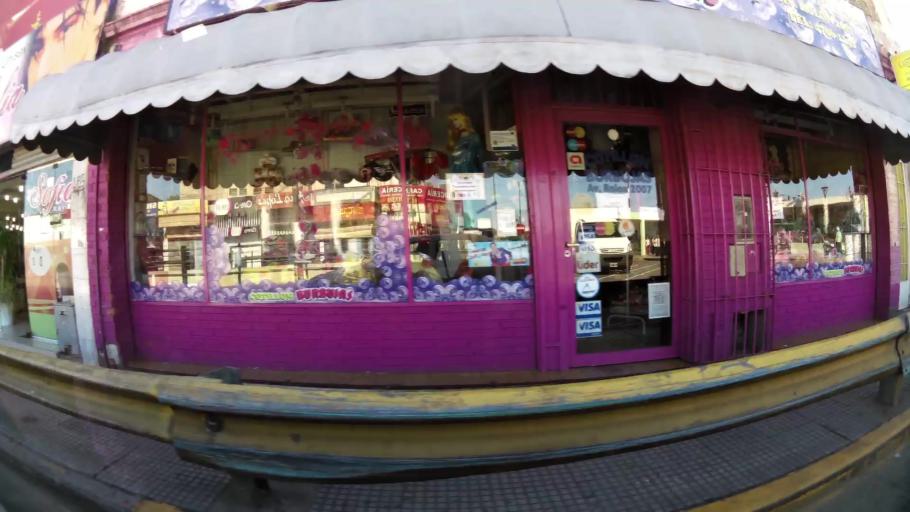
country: AR
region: Buenos Aires
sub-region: Partido de San Isidro
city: San Isidro
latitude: -34.5087
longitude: -58.5660
